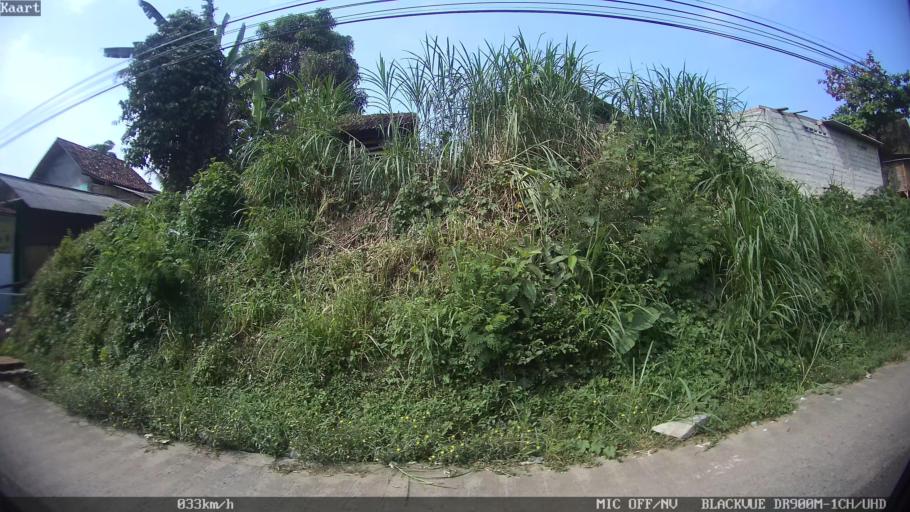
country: ID
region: Lampung
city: Gedongtataan
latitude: -5.3671
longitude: 105.1544
